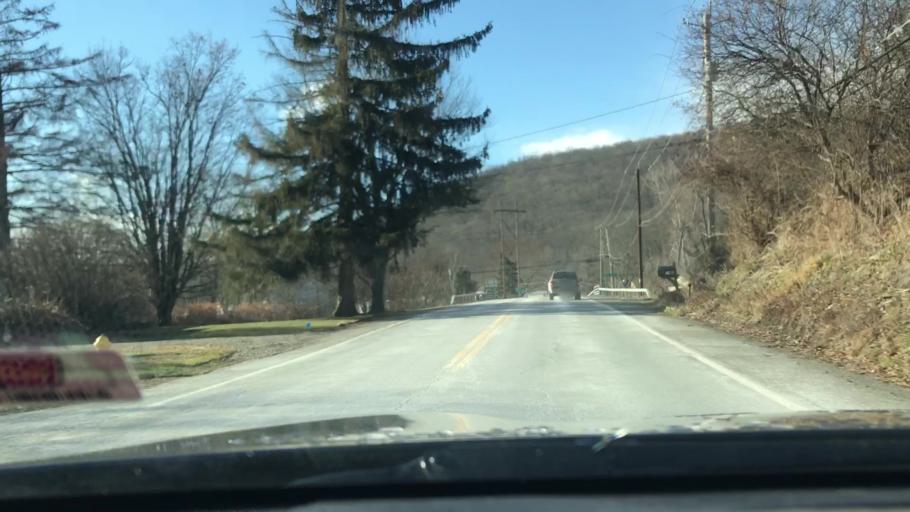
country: US
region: New York
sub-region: Chemung County
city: Big Flats
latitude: 42.1601
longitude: -76.9224
